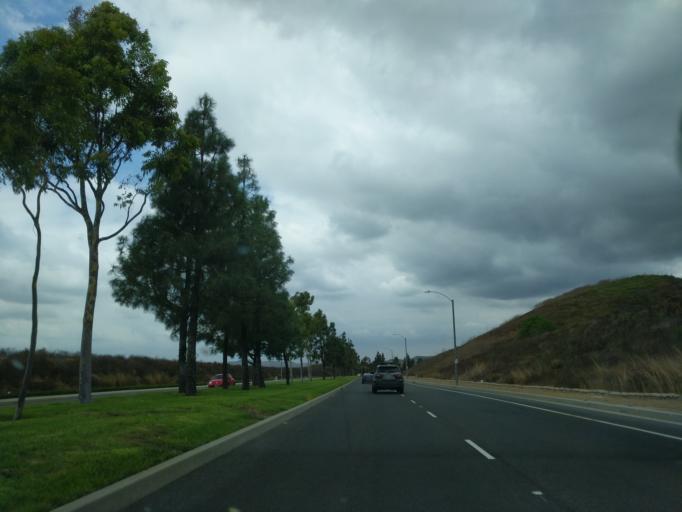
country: US
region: California
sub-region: Orange County
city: North Tustin
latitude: 33.7760
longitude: -117.7592
